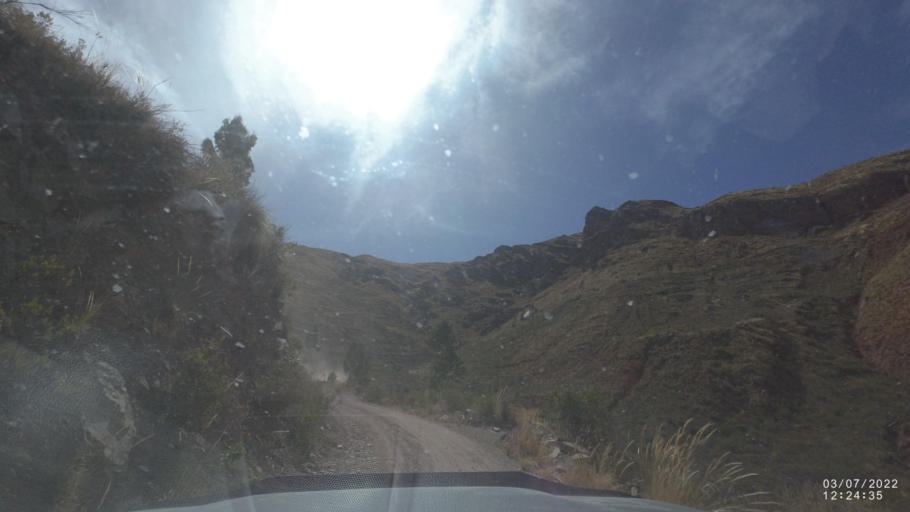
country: BO
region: Cochabamba
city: Irpa Irpa
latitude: -17.8126
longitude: -66.6173
